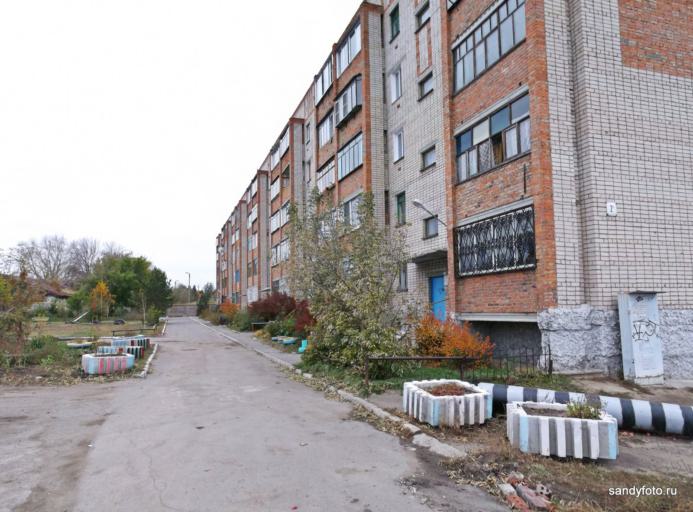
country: RU
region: Chelyabinsk
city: Troitsk
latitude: 54.0866
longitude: 61.5361
